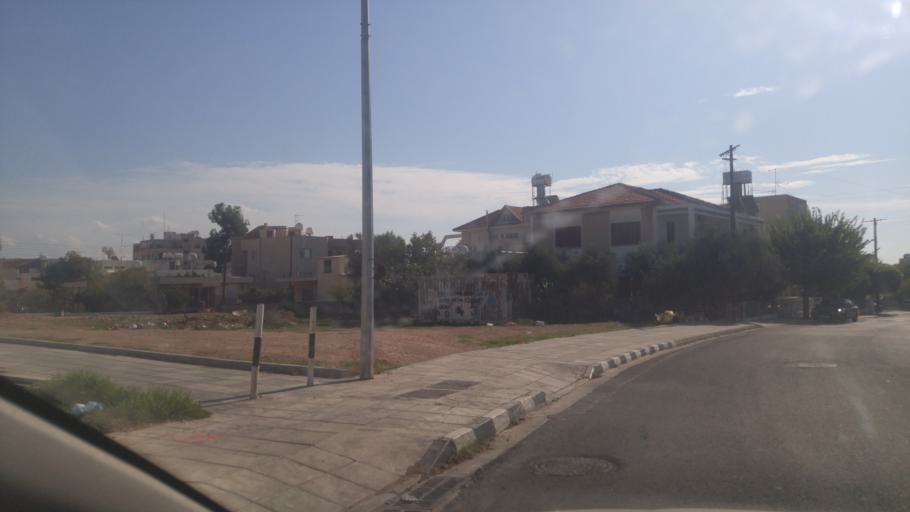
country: CY
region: Limassol
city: Limassol
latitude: 34.6937
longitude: 33.0489
